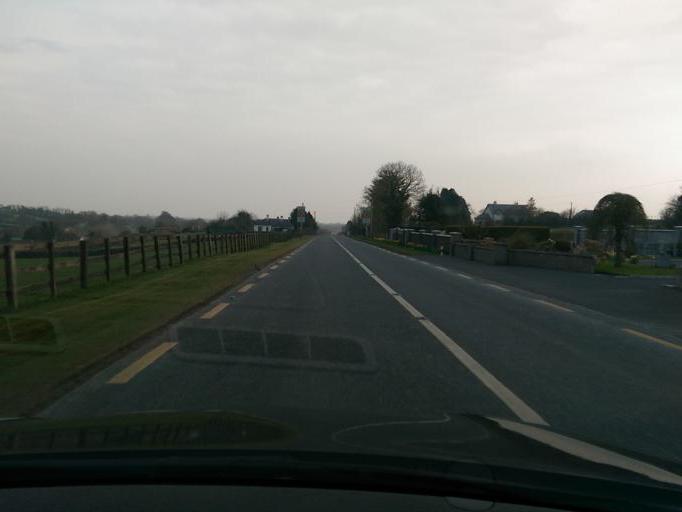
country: IE
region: Leinster
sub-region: An Iarmhi
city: Athlone
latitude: 53.4804
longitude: -7.8603
